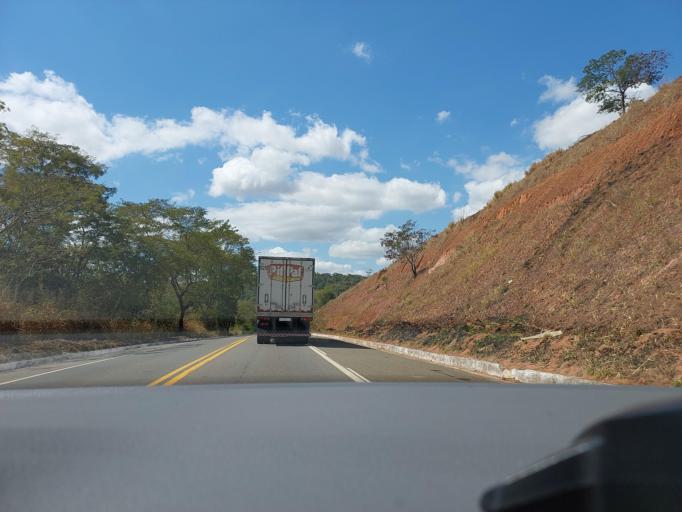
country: BR
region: Minas Gerais
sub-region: Muriae
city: Muriae
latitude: -21.1224
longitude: -42.2151
